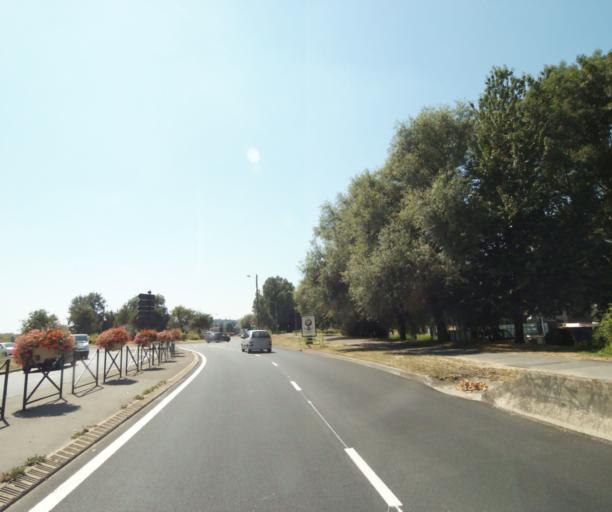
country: FR
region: Ile-de-France
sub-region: Departement de Seine-et-Marne
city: Saint-Thibault-des-Vignes
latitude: 48.8664
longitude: 2.6781
